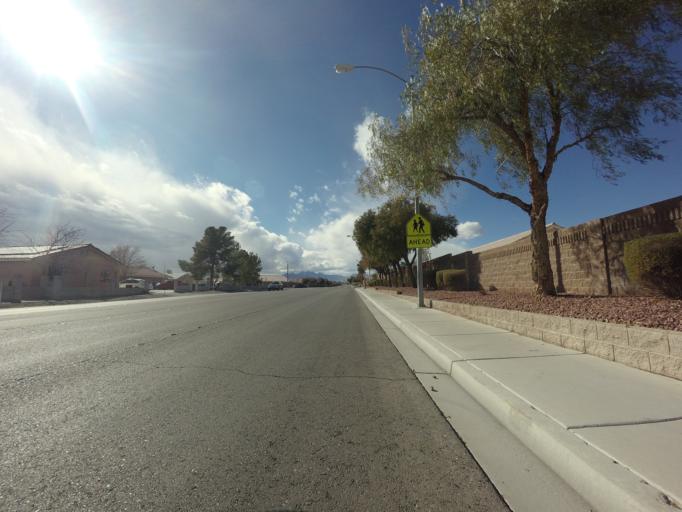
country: US
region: Nevada
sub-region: Clark County
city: North Las Vegas
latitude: 36.2543
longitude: -115.1248
